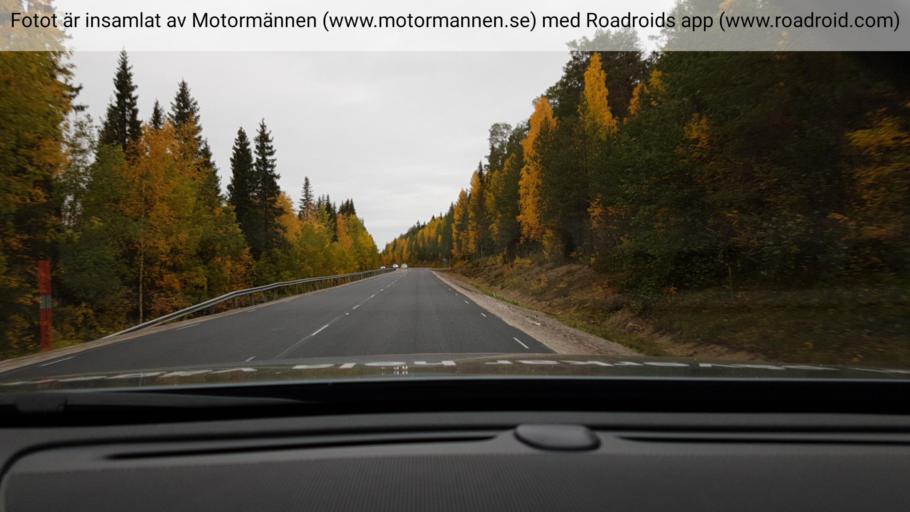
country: SE
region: Norrbotten
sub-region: Overkalix Kommun
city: OEverkalix
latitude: 66.4726
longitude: 22.7907
